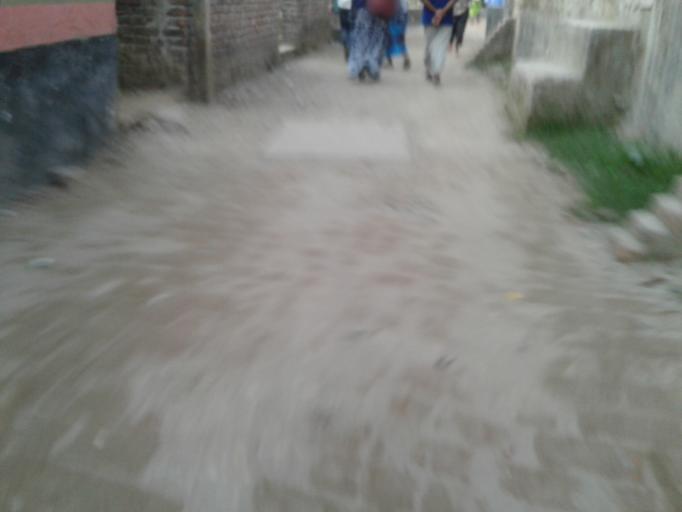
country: BD
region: Dhaka
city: Azimpur
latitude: 23.7053
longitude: 90.3564
